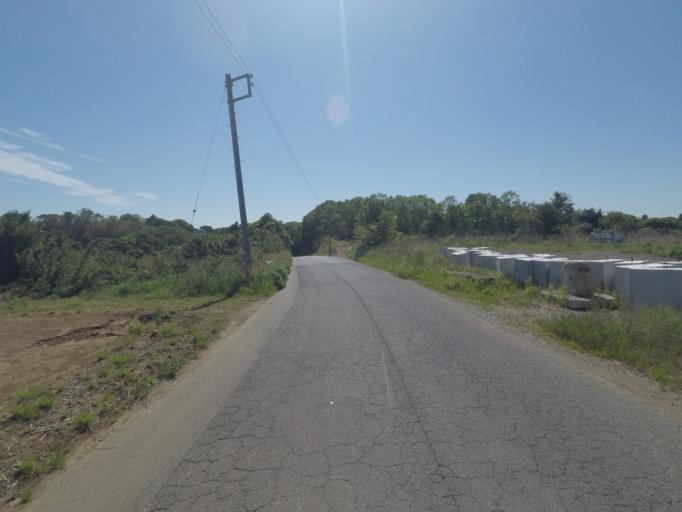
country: JP
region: Ibaraki
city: Itako
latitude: 36.0259
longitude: 140.4792
